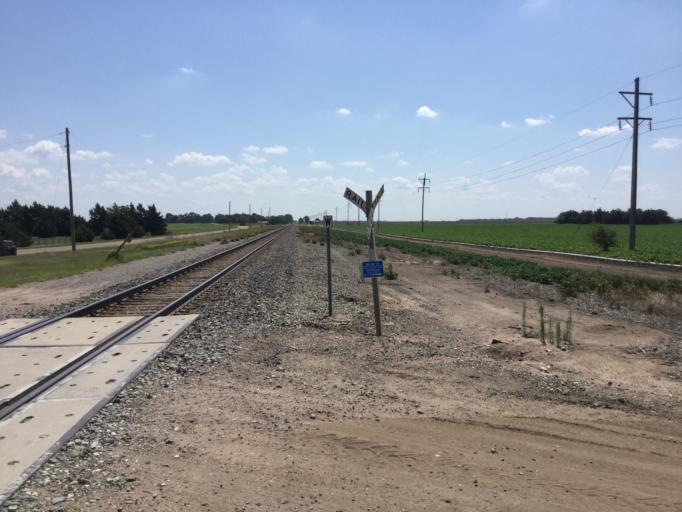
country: US
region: Kansas
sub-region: Harvey County
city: Halstead
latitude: 38.0144
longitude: -97.5968
